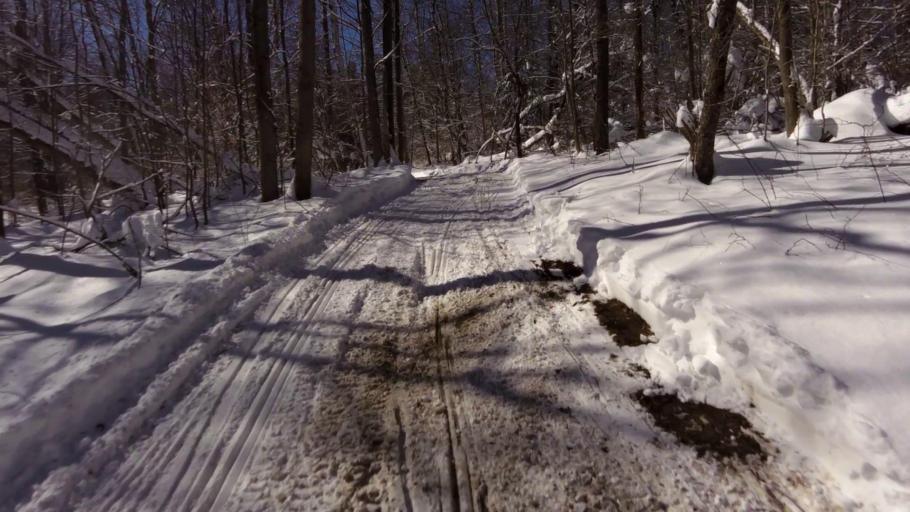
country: US
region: New York
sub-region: Chautauqua County
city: Mayville
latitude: 42.2274
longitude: -79.4087
